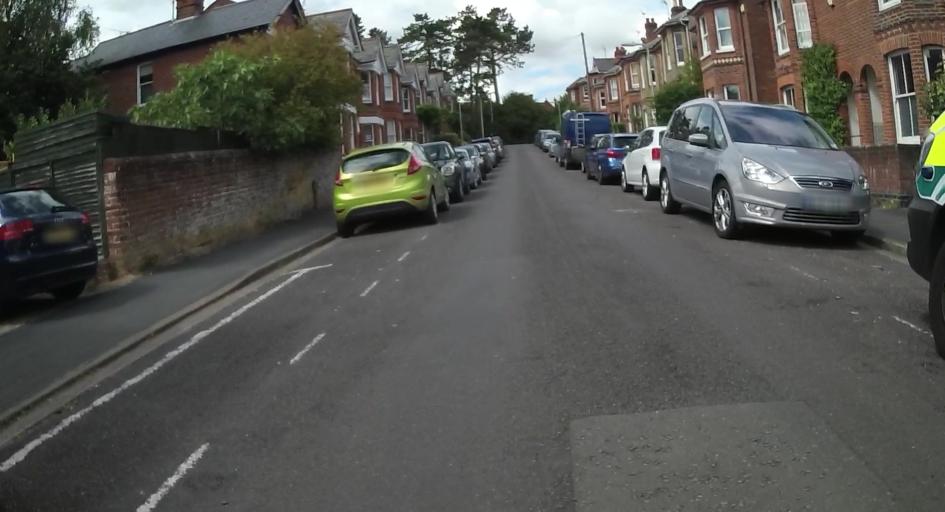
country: GB
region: England
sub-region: Hampshire
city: Winchester
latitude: 51.0687
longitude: -1.3211
